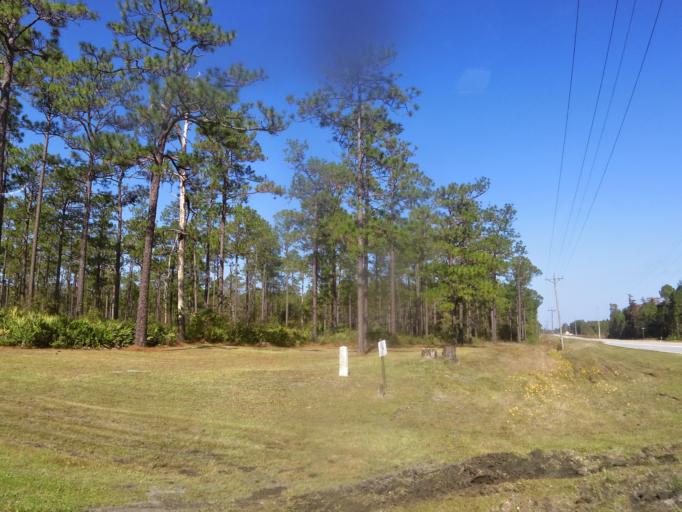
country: US
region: Georgia
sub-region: Charlton County
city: Folkston
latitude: 30.7402
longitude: -82.0715
